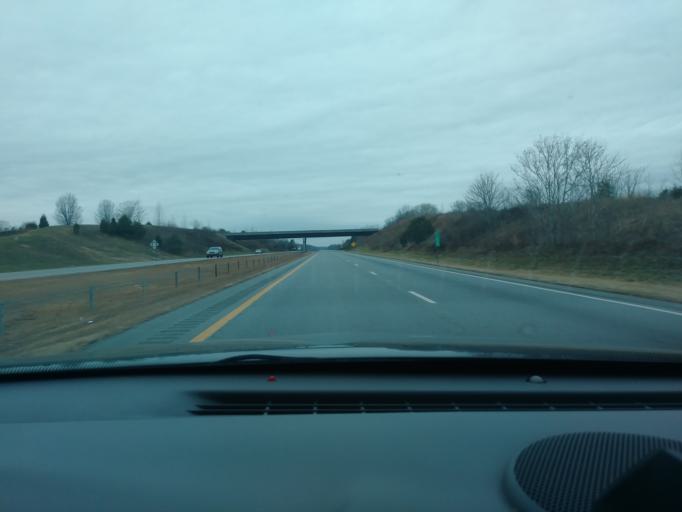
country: US
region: North Carolina
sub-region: Yadkin County
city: Yadkinville
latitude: 36.1196
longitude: -80.7004
